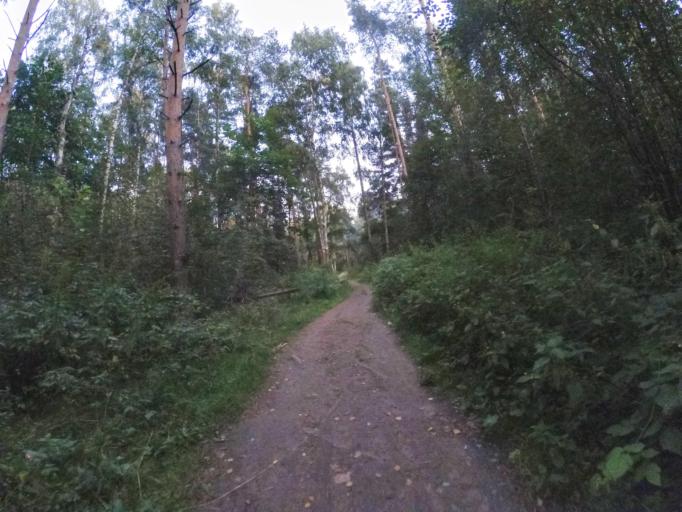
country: RU
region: Moscow
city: Zhulebino
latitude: 55.6732
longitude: 37.8490
